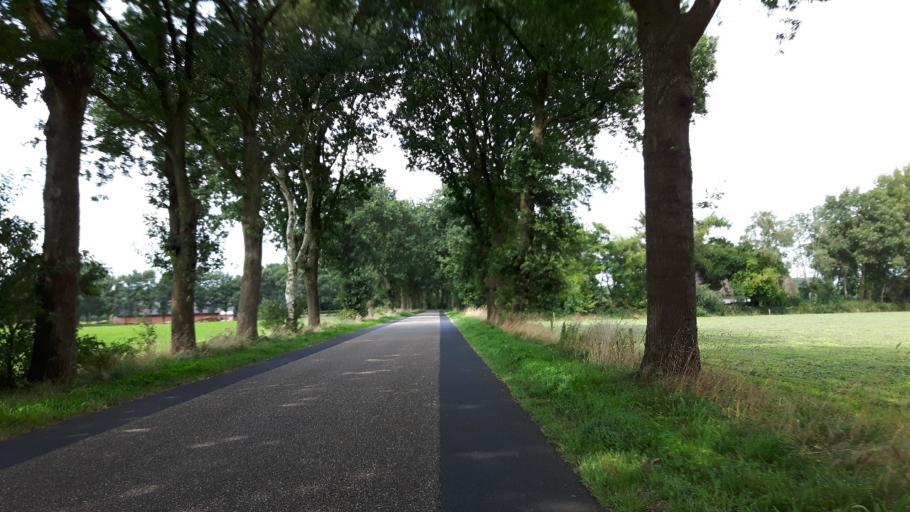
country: NL
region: Groningen
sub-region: Gemeente Leek
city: Leek
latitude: 53.0858
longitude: 6.3187
